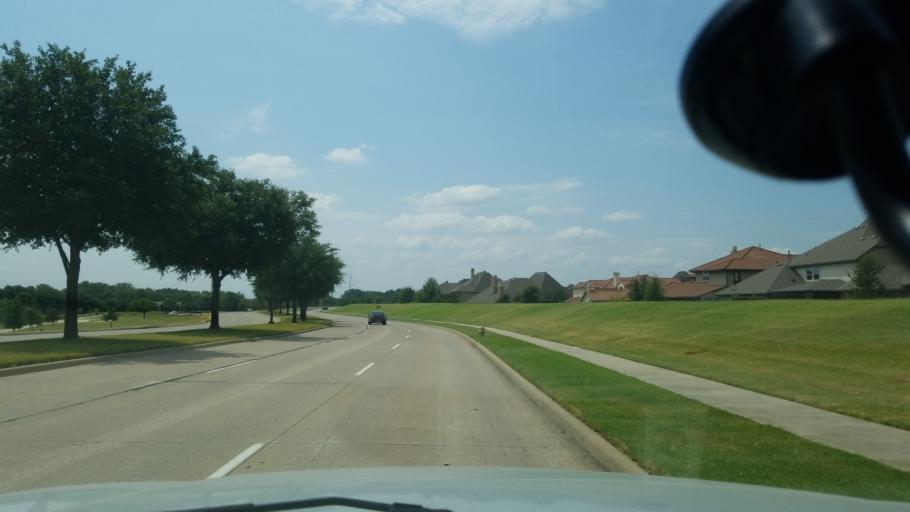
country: US
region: Texas
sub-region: Dallas County
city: Farmers Branch
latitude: 32.8833
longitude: -96.9334
